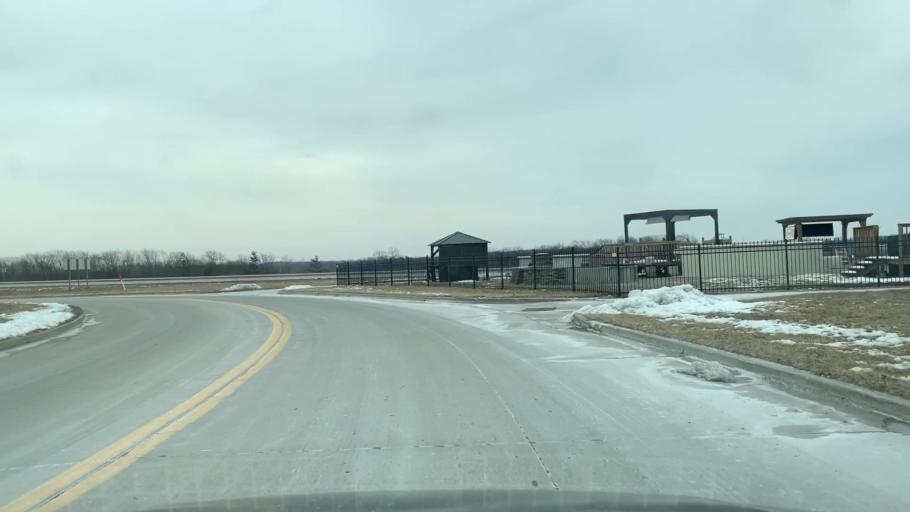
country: US
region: Missouri
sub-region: Jackson County
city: Lees Summit
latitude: 38.9544
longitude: -94.3618
